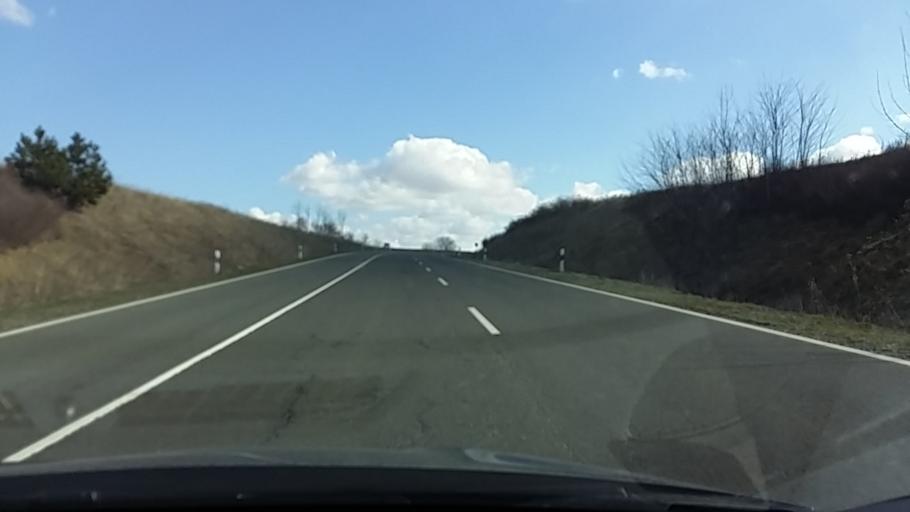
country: HU
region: Baranya
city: Kozarmisleny
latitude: 46.0226
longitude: 18.2833
